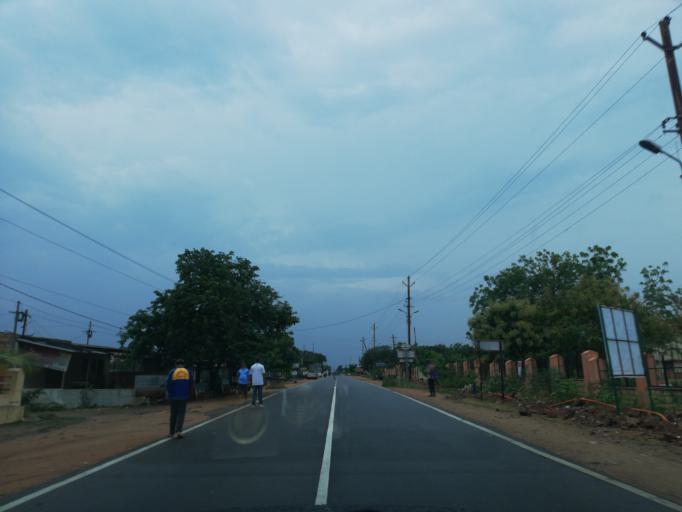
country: IN
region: Andhra Pradesh
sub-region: Guntur
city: Macherla
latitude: 16.6123
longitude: 79.2978
